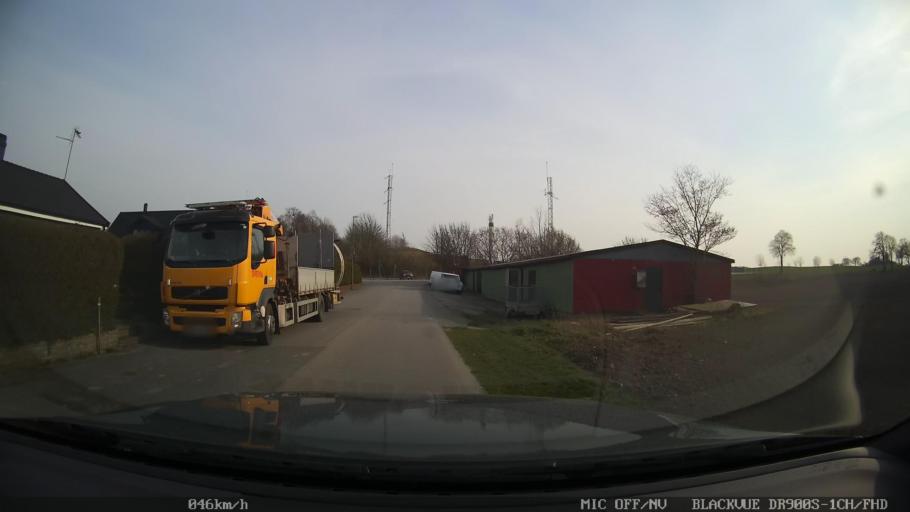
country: SE
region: Skane
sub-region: Ystads Kommun
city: Ystad
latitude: 55.4510
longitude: 13.7955
